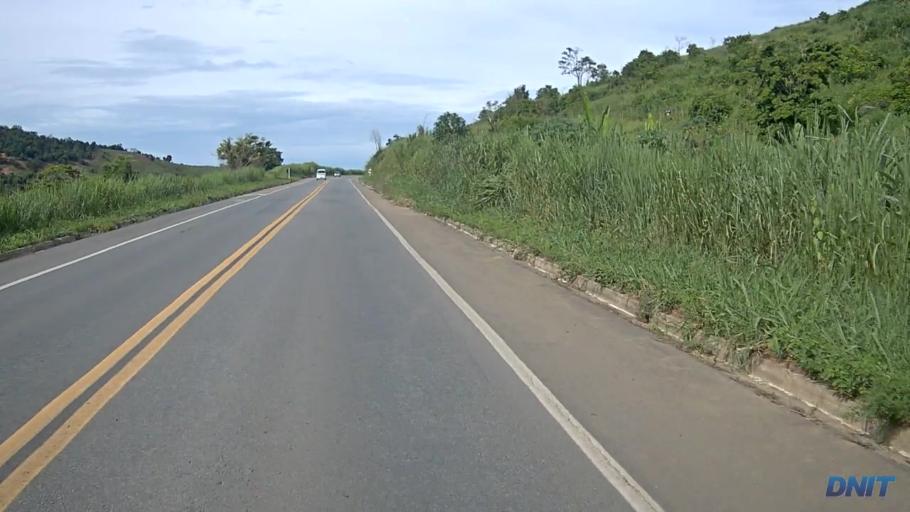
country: BR
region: Minas Gerais
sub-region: Belo Oriente
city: Belo Oriente
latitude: -19.1999
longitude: -42.2872
